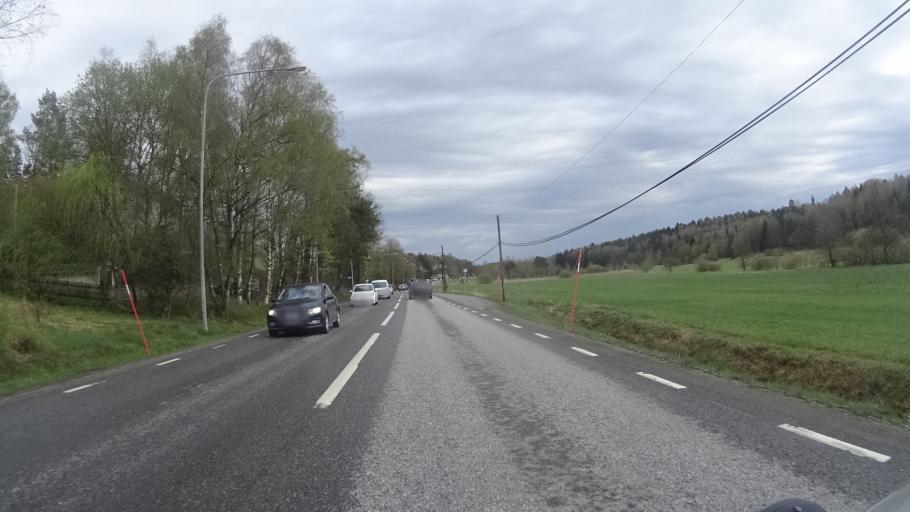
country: SE
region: Stockholm
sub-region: Botkyrka Kommun
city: Tullinge
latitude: 59.2344
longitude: 17.9223
